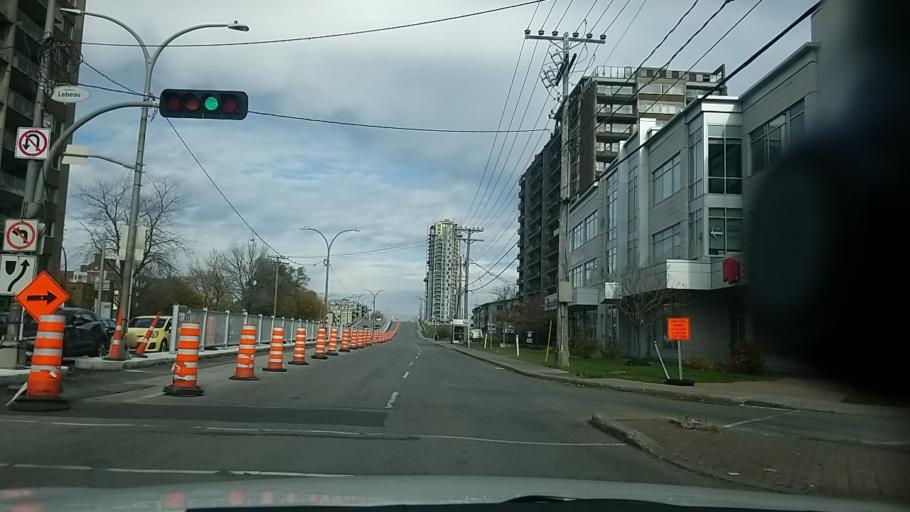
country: CA
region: Quebec
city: Mont-Royal
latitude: 45.5288
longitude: -73.6689
